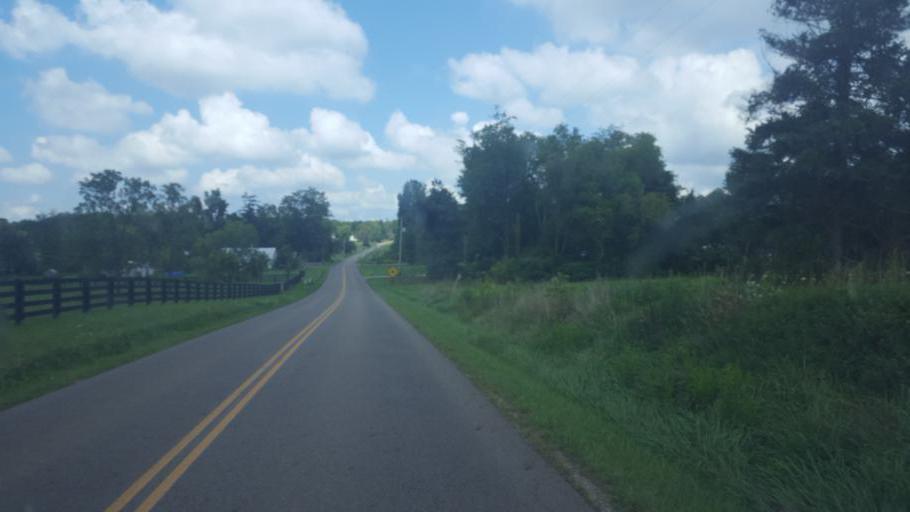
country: US
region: Ohio
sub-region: Knox County
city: Mount Vernon
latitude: 40.4475
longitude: -82.4869
